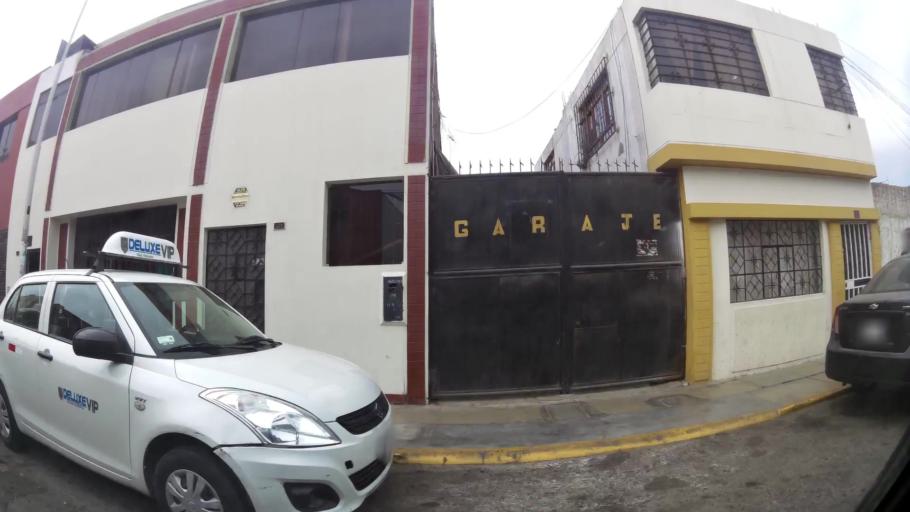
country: PE
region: La Libertad
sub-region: Provincia de Trujillo
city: Trujillo
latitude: -8.1158
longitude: -79.0290
